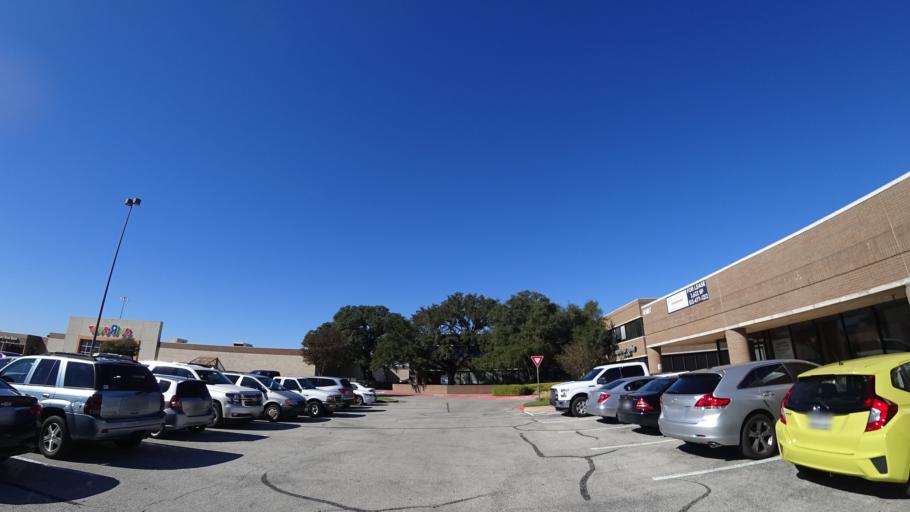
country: US
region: Texas
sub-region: Travis County
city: Rollingwood
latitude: 30.2379
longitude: -97.7967
